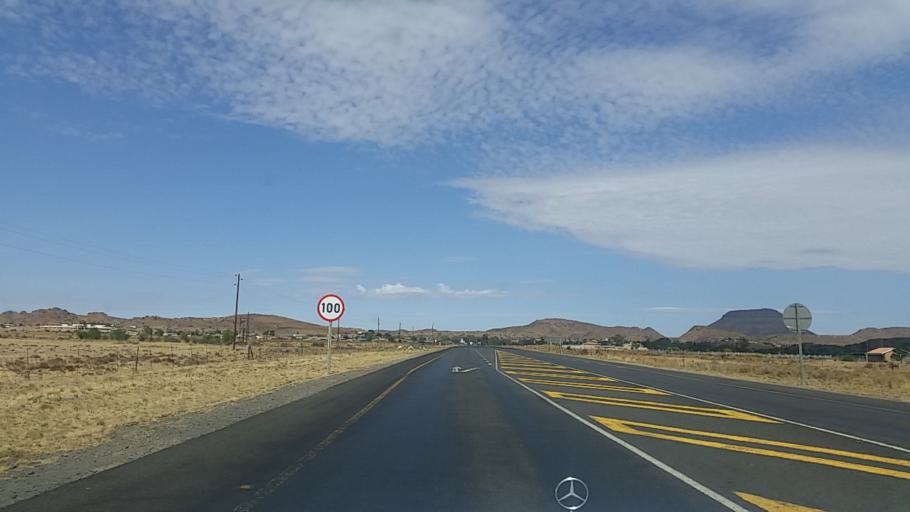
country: ZA
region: Northern Cape
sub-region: Pixley ka Seme District Municipality
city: Colesberg
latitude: -30.7026
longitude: 25.1210
